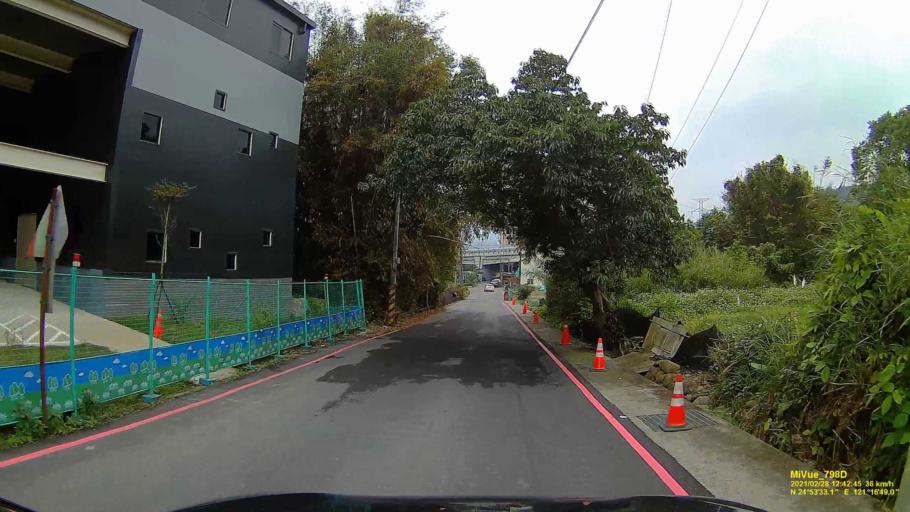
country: TW
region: Taiwan
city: Daxi
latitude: 24.8923
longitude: 121.2803
